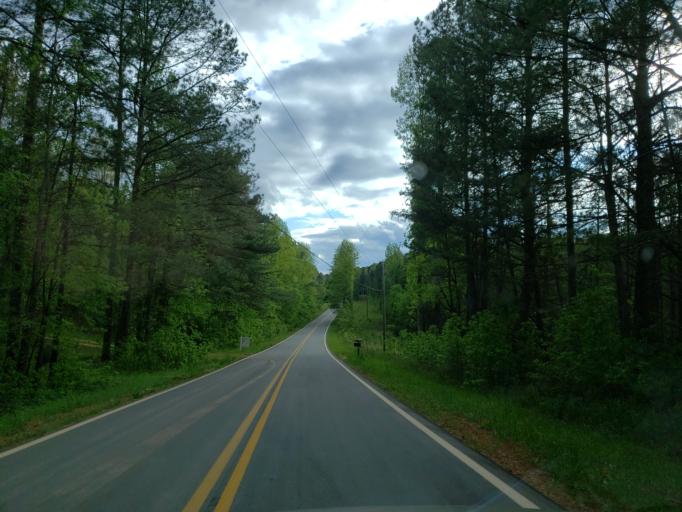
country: US
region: Georgia
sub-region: Haralson County
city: Tallapoosa
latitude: 33.8608
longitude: -85.3661
